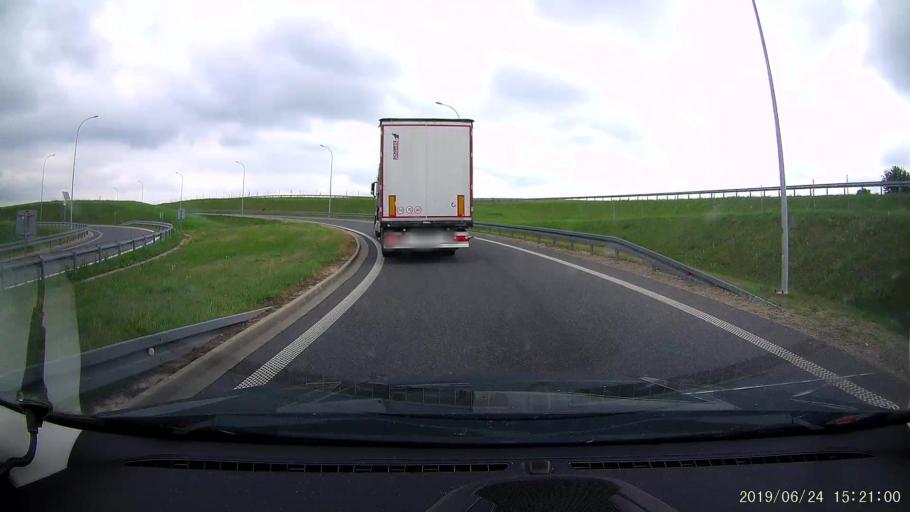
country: PL
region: Subcarpathian Voivodeship
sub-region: Powiat przeworski
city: Mirocin
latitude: 50.0358
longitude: 22.5773
